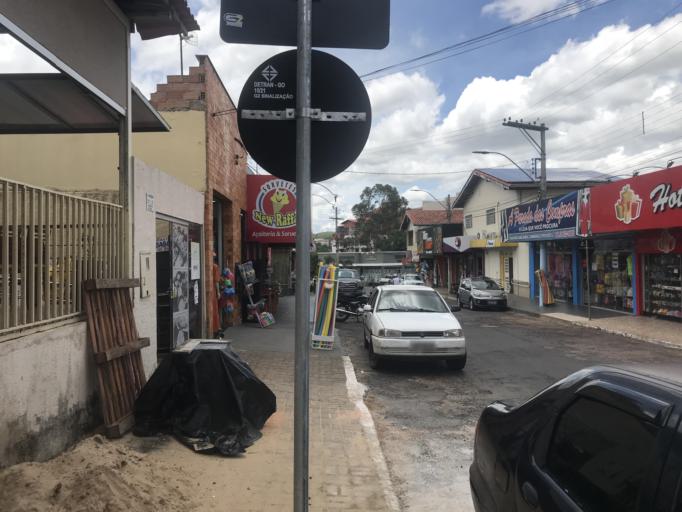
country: BR
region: Goias
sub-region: Caldas Novas
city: Caldas Novas
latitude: -17.7703
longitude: -48.7552
